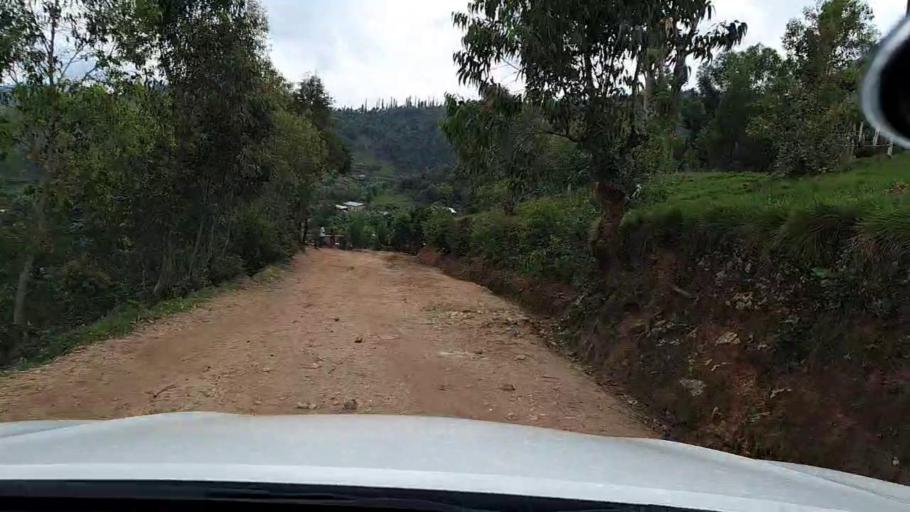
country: RW
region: Western Province
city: Kibuye
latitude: -2.1872
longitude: 29.2950
